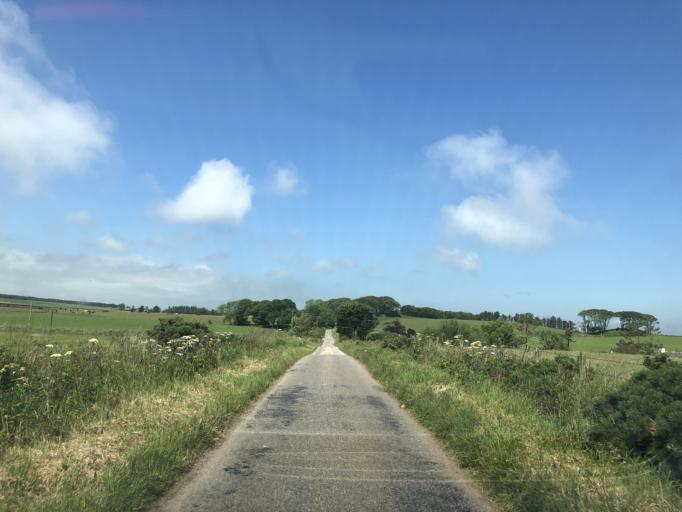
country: GB
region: Scotland
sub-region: Aberdeenshire
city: Stonehaven
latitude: 56.9147
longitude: -2.2034
